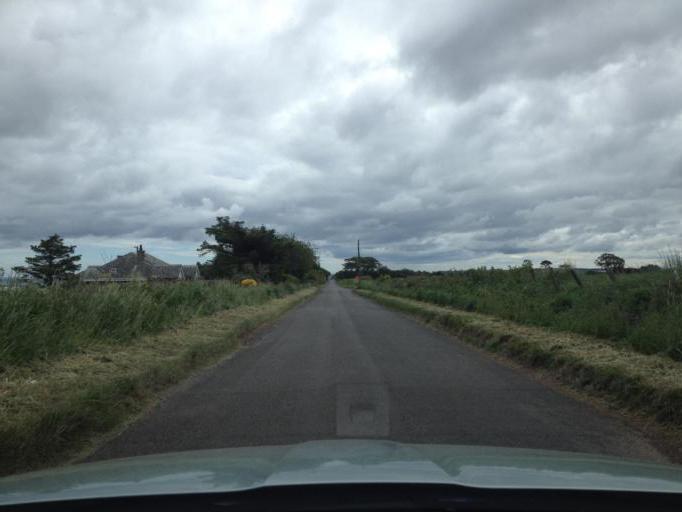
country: GB
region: Scotland
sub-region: Fife
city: Strathkinness
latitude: 56.3372
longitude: -2.8915
